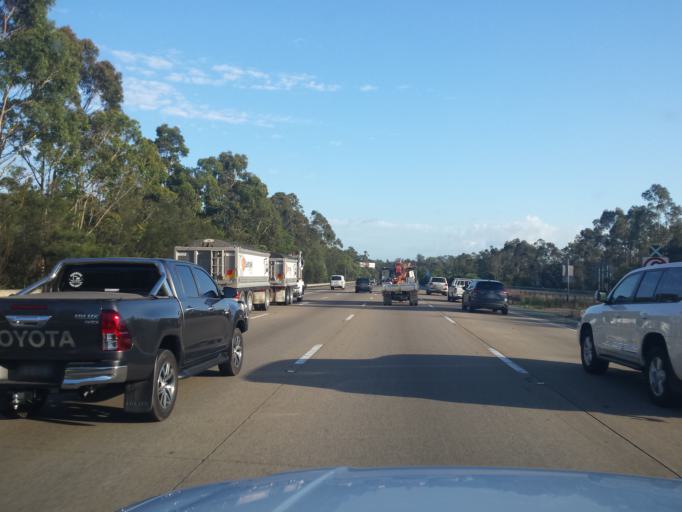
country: AU
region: Queensland
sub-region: Gold Coast
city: Oxenford
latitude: -27.8384
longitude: 153.3031
